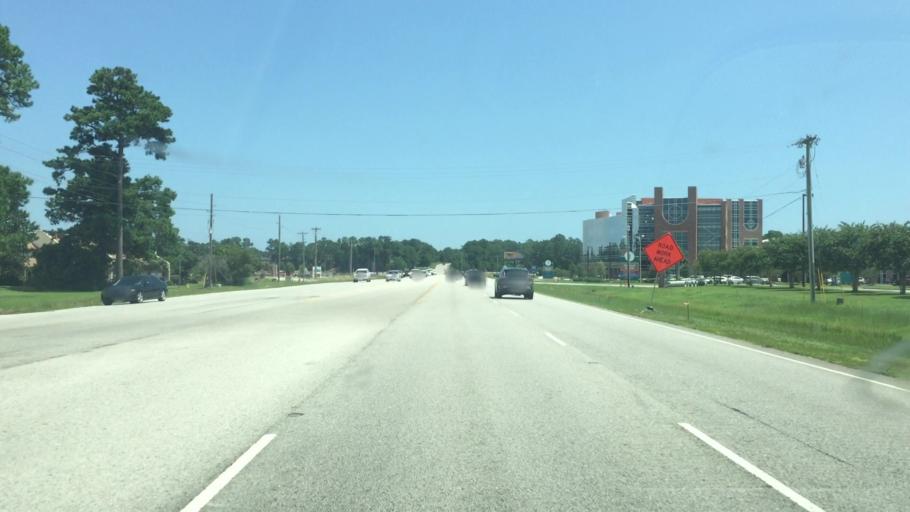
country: US
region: South Carolina
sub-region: Horry County
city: Little River
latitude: 33.8678
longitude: -78.6654
